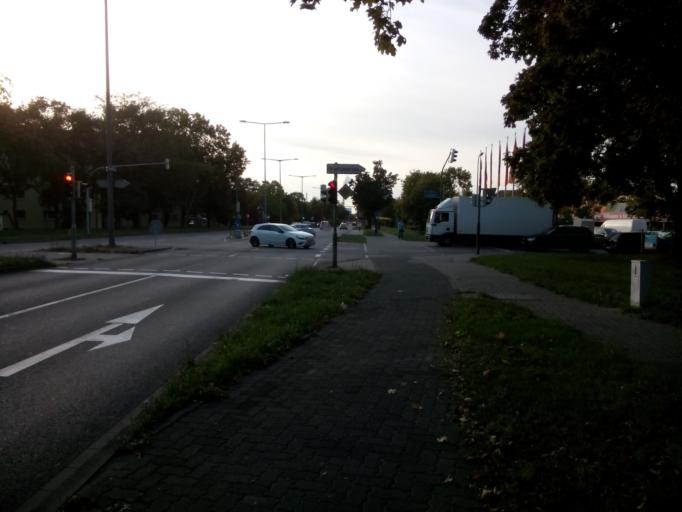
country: DE
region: Baden-Wuerttemberg
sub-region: Karlsruhe Region
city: Karlsruhe
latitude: 48.9974
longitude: 8.3566
